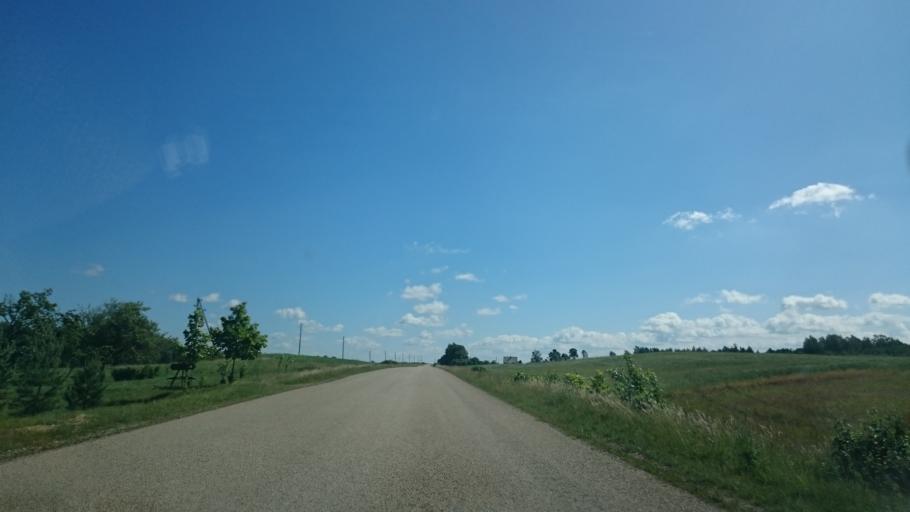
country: LV
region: Cibla
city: Cibla
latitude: 56.5324
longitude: 27.8411
